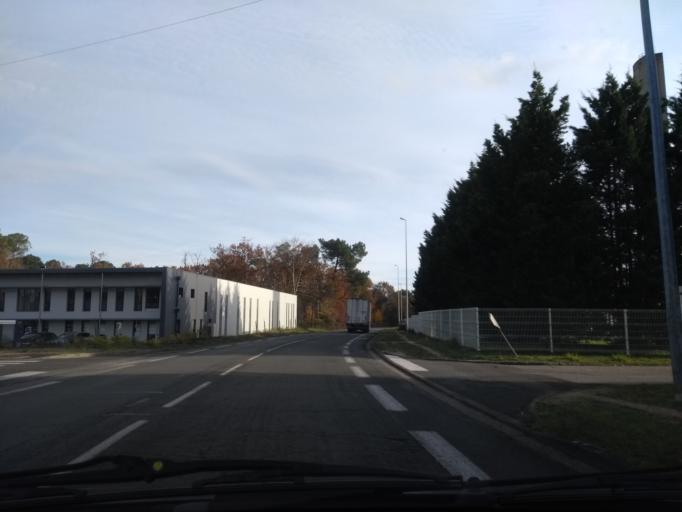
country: FR
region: Aquitaine
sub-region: Departement de la Gironde
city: Pessac
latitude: 44.7894
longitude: -0.6628
